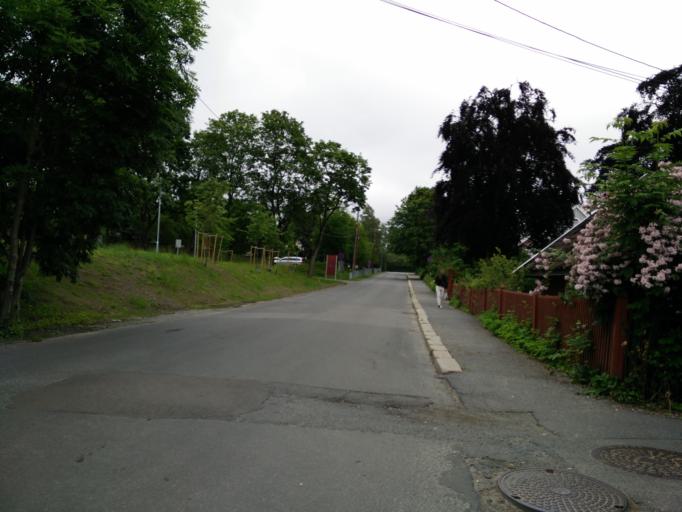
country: NO
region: Oslo
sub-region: Oslo
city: Sjolyststranda
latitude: 59.9348
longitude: 10.7016
